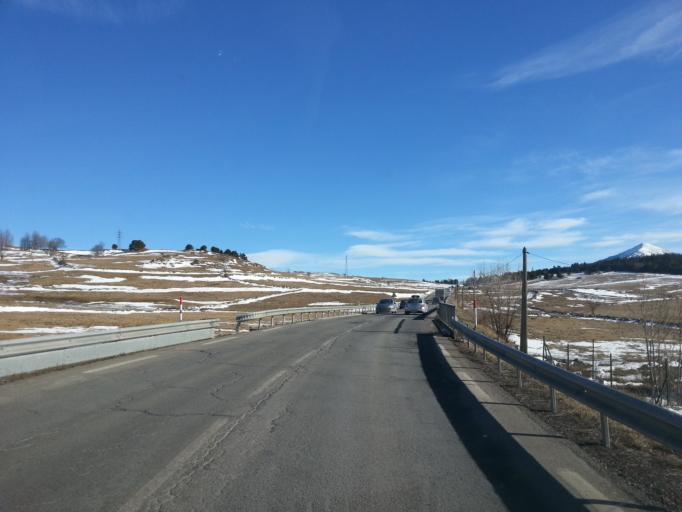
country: ES
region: Catalonia
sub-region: Provincia de Girona
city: Llivia
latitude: 42.4945
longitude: 2.0799
